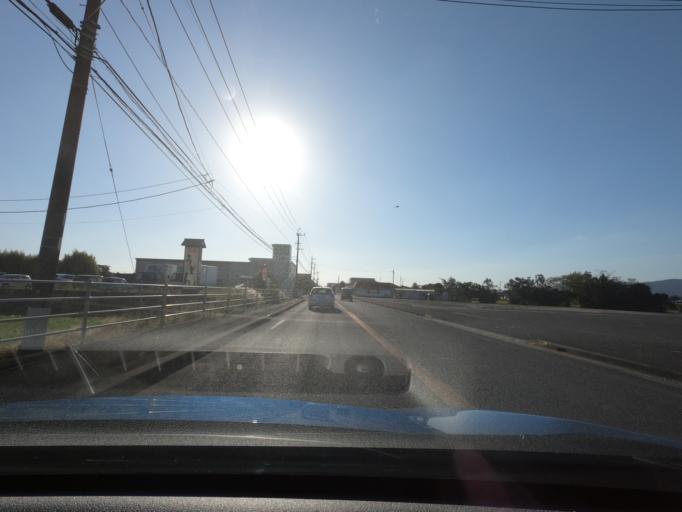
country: JP
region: Kagoshima
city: Izumi
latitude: 32.1014
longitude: 130.3104
